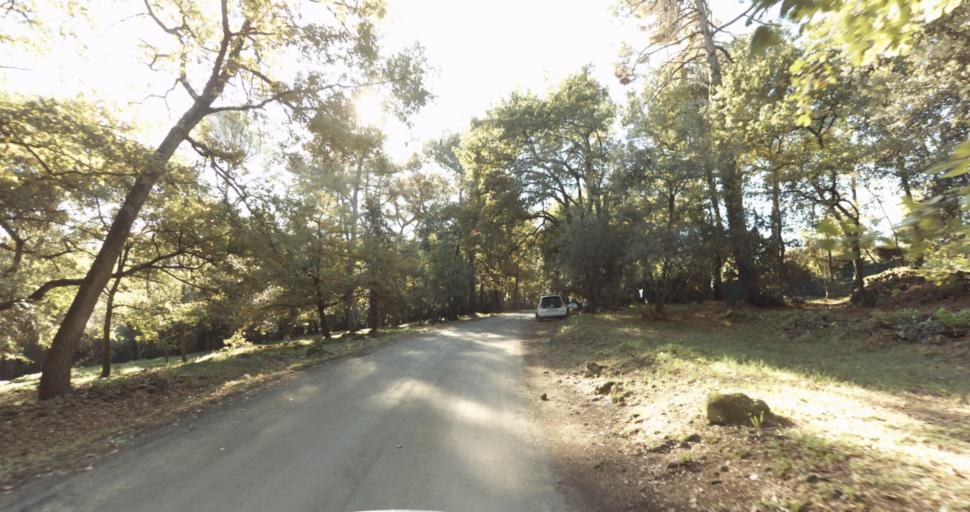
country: FR
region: Provence-Alpes-Cote d'Azur
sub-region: Departement des Alpes-Maritimes
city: Vence
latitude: 43.7086
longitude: 7.0958
